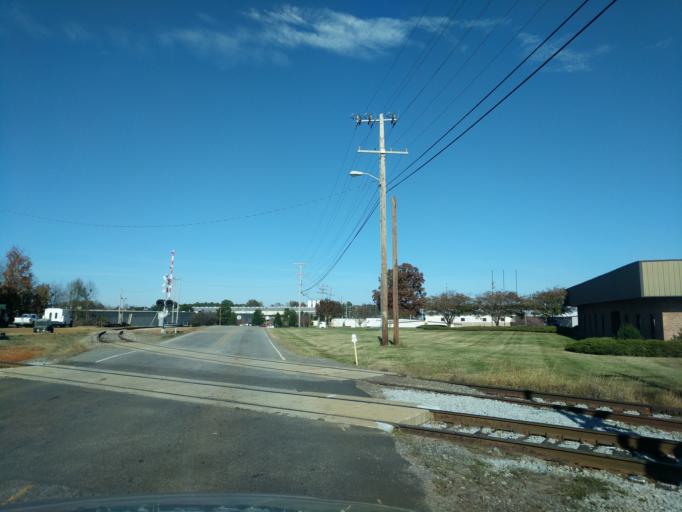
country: US
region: North Carolina
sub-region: Iredell County
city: Statesville
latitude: 35.7906
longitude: -80.9229
